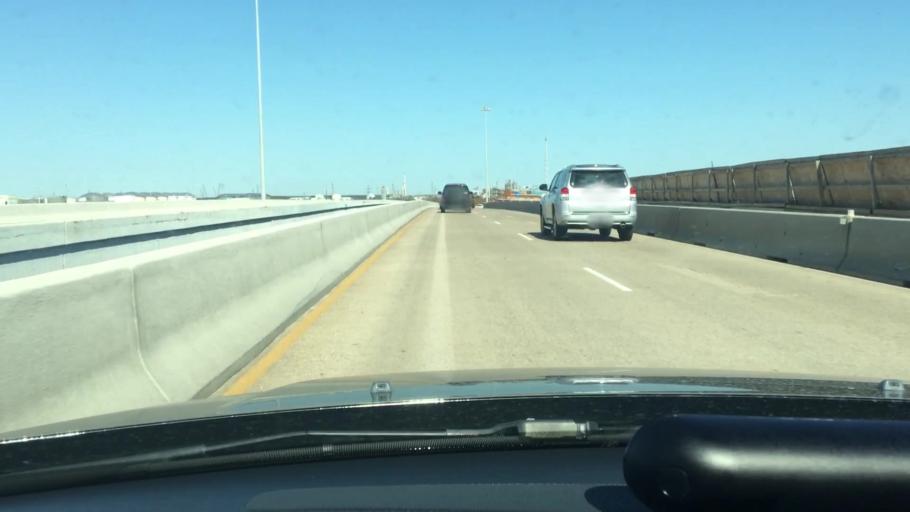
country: US
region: Texas
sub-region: Harris County
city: Deer Park
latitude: 29.7119
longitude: -95.1534
